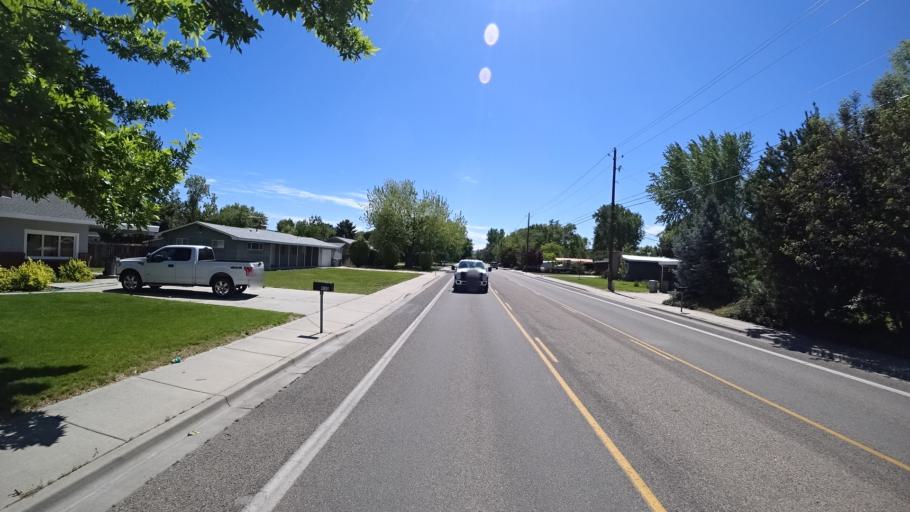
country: US
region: Idaho
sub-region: Ada County
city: Boise
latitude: 43.5775
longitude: -116.1712
